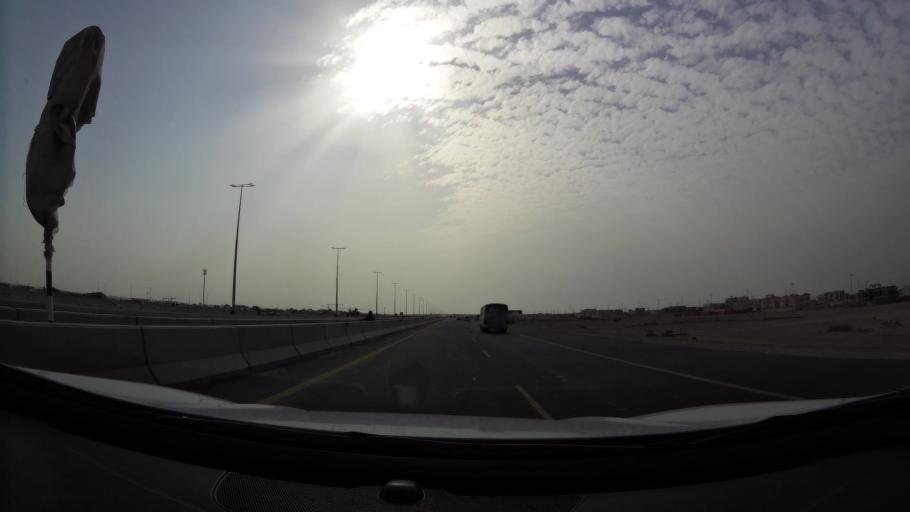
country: AE
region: Abu Dhabi
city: Abu Dhabi
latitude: 24.2979
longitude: 54.5810
